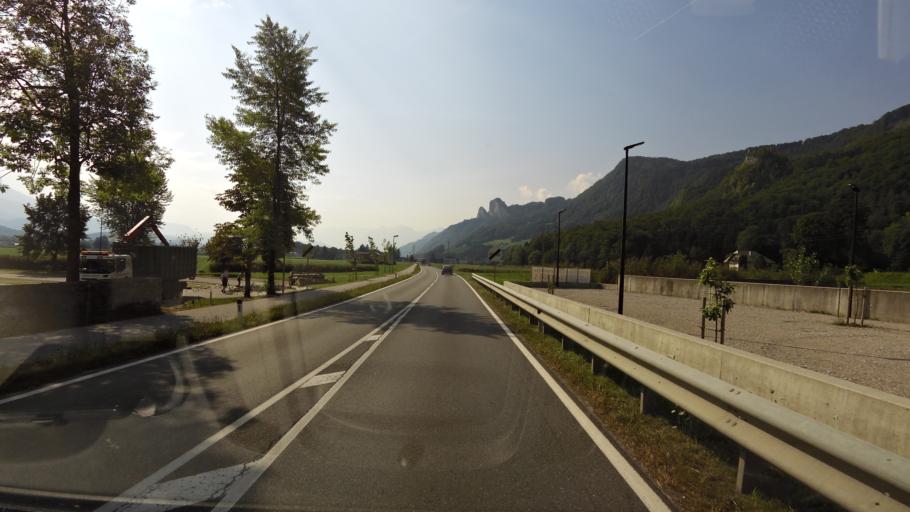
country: DE
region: Bavaria
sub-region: Upper Bavaria
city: Marktschellenberg
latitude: 47.7154
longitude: 13.0622
